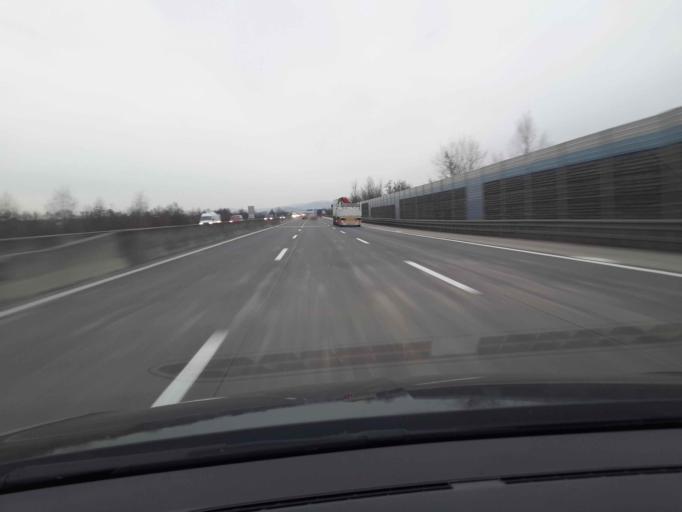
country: AT
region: Lower Austria
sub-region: Politischer Bezirk Amstetten
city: Sankt Valentin
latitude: 48.1843
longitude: 14.5385
